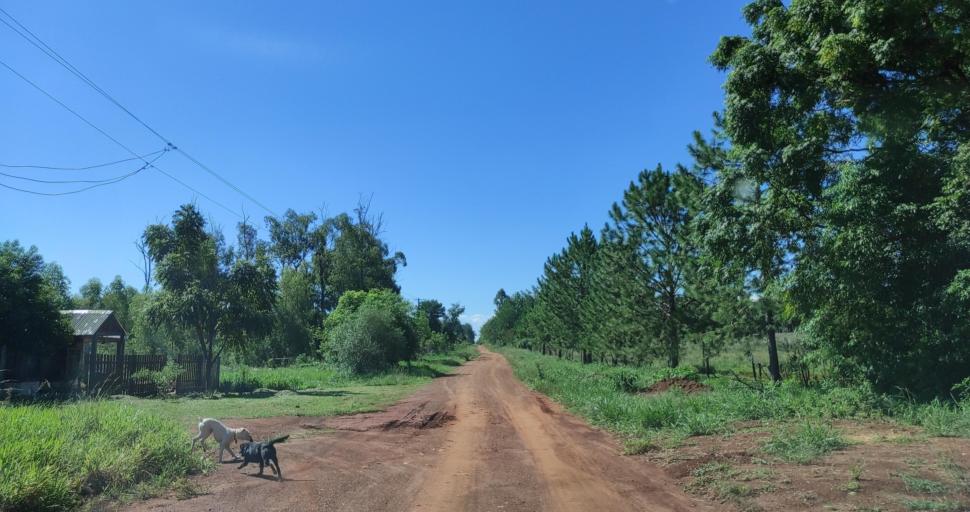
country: AR
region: Misiones
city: Garupa
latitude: -27.4731
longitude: -55.7985
